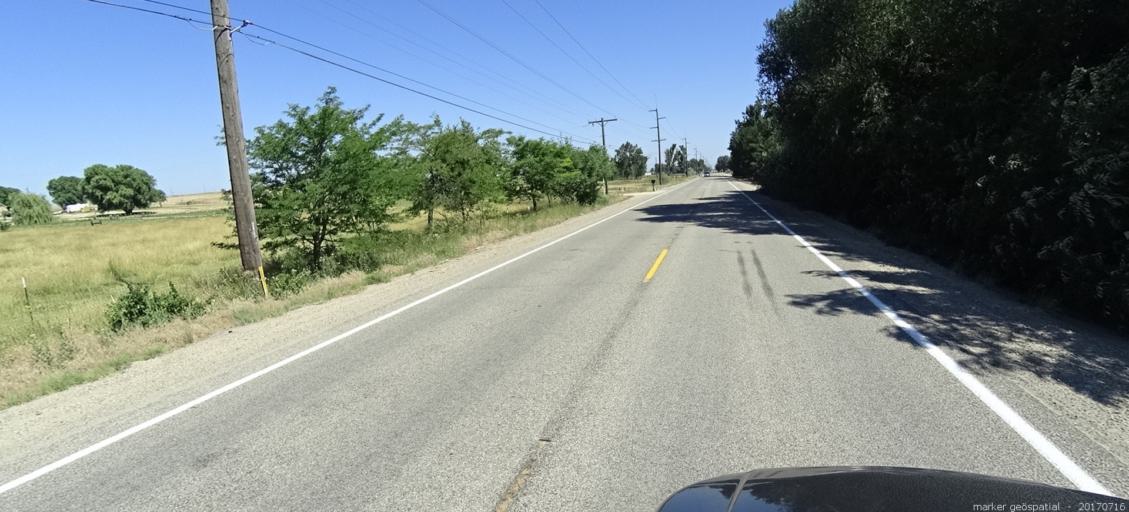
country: US
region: Idaho
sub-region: Ada County
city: Kuna
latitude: 43.5255
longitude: -116.3344
